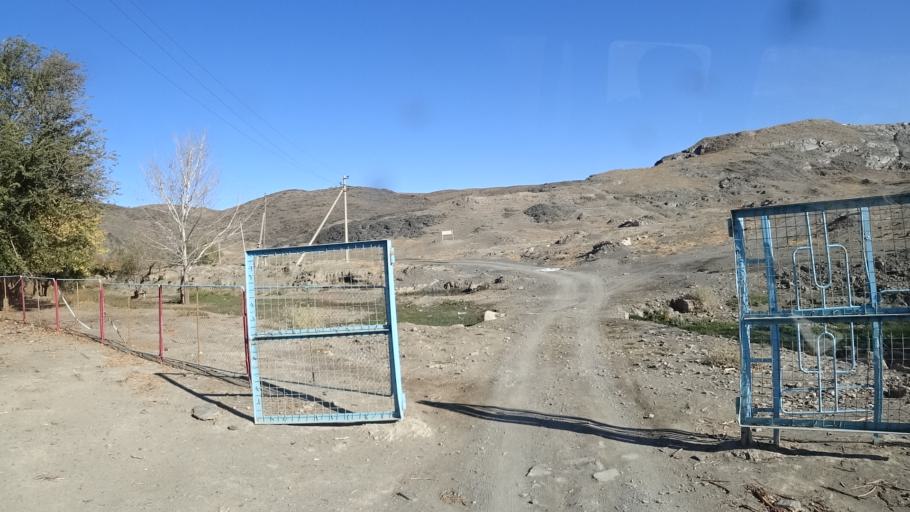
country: UZ
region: Navoiy
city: Nurota
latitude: 40.2971
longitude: 65.6057
